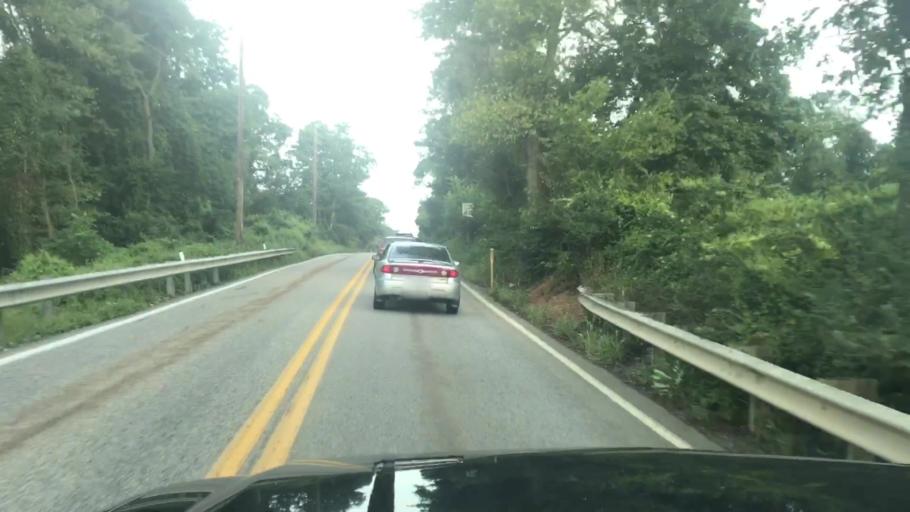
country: US
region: Pennsylvania
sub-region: Cumberland County
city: Shiremanstown
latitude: 40.1988
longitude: -76.9478
